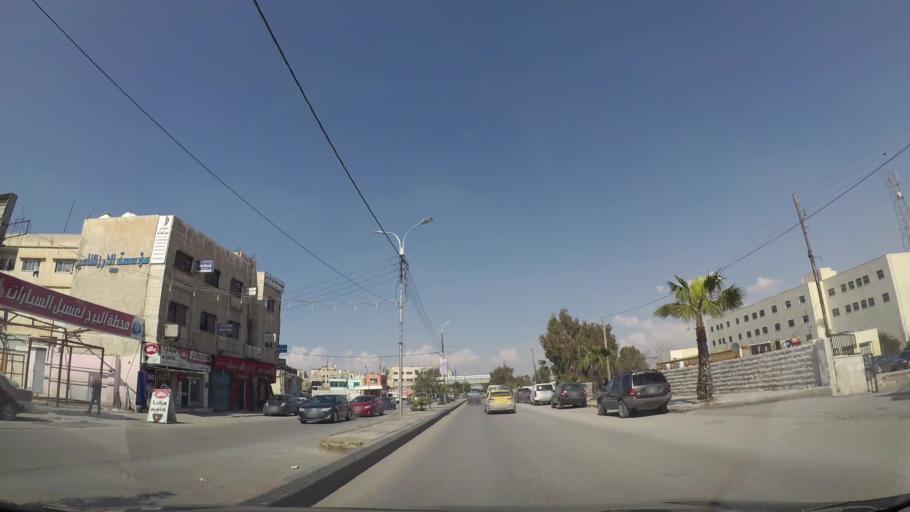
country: JO
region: Zarqa
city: Zarqa
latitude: 32.0671
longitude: 36.0962
